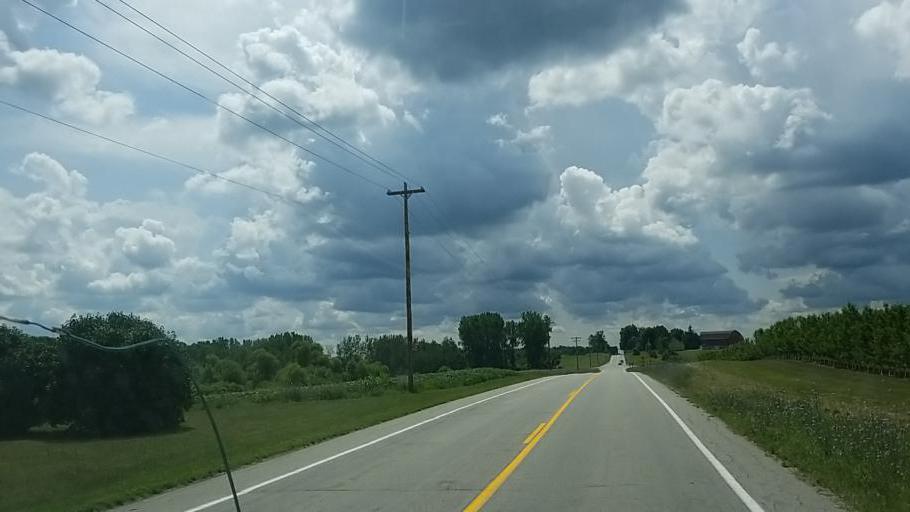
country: US
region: Michigan
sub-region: Kent County
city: Walker
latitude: 43.0771
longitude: -85.7681
